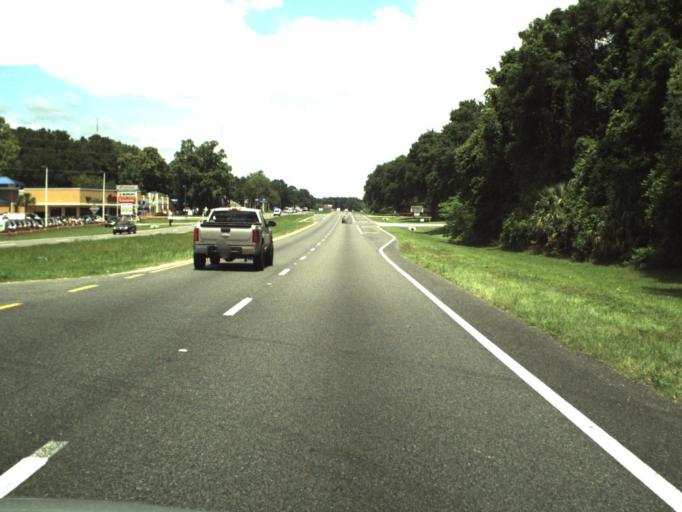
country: US
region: Florida
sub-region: Marion County
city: Ocala
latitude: 29.2257
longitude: -82.1481
